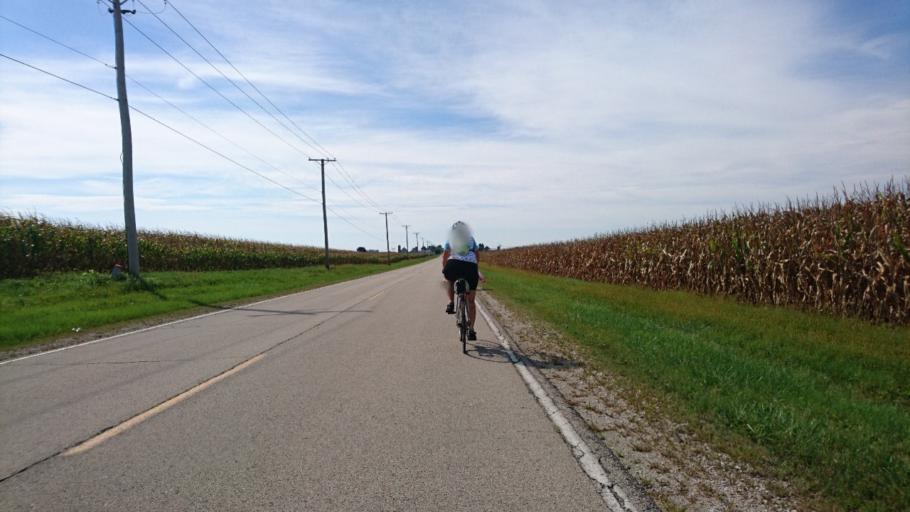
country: US
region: Illinois
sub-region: Will County
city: Elwood
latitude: 41.4138
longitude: -88.0780
